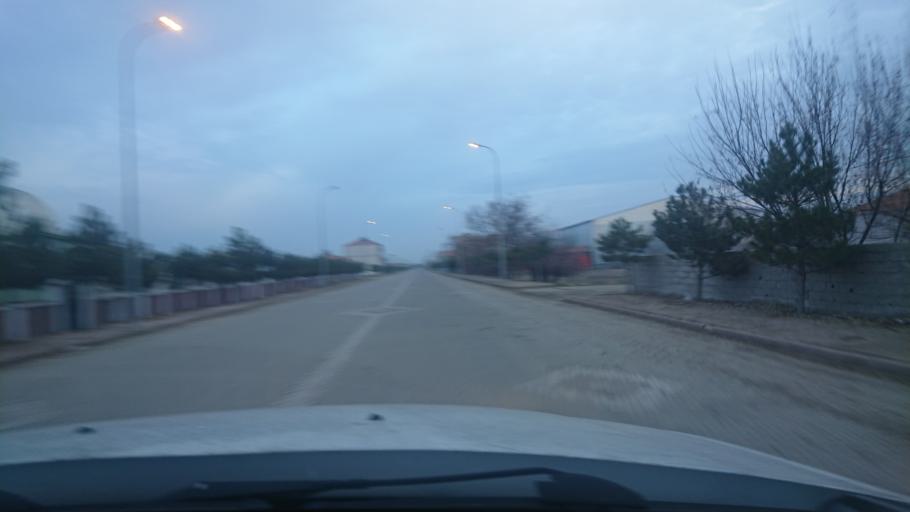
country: TR
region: Aksaray
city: Yesilova
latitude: 38.3333
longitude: 33.7518
